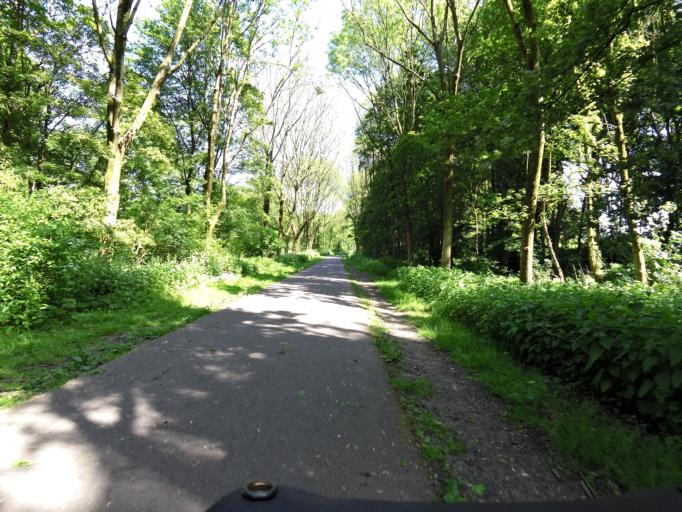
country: NL
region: South Holland
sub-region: Gemeente Barendrecht
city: Barendrecht
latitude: 51.8335
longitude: 4.5237
